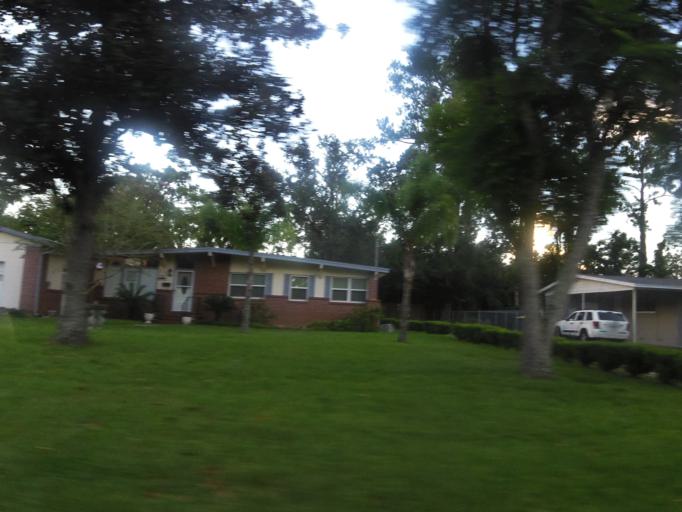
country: US
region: Florida
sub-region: Duval County
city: Jacksonville
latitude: 30.2344
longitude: -81.6159
